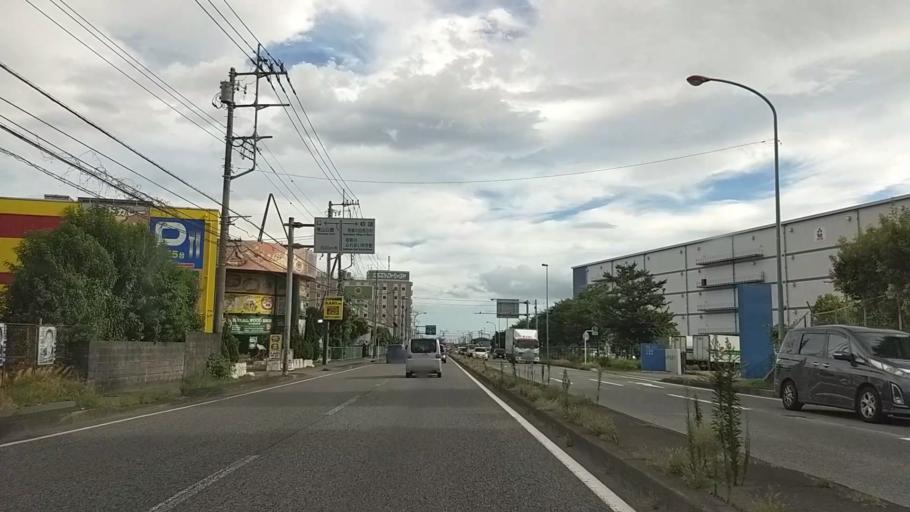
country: JP
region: Kanagawa
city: Zama
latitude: 35.5612
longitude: 139.3466
